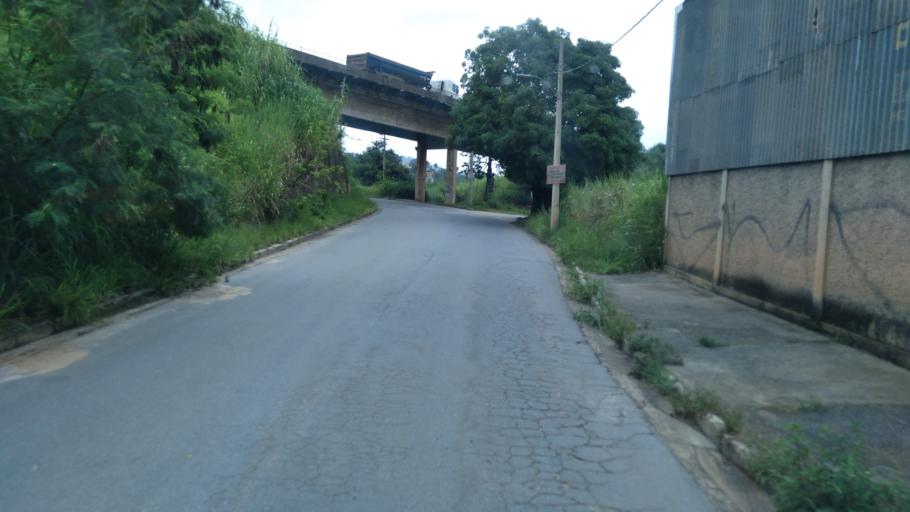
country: BR
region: Minas Gerais
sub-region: Santa Luzia
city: Santa Luzia
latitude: -19.8416
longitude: -43.8728
